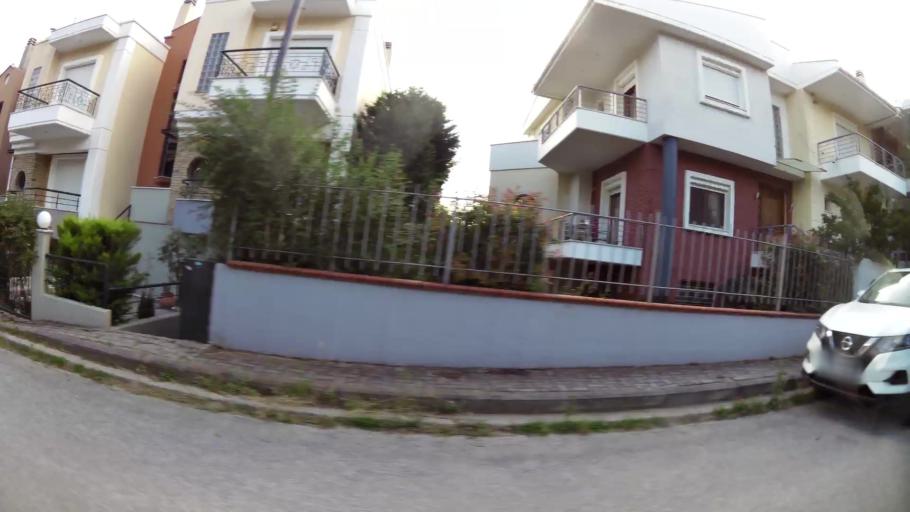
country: GR
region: Central Macedonia
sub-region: Nomos Thessalonikis
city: Pefka
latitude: 40.6530
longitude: 22.9999
